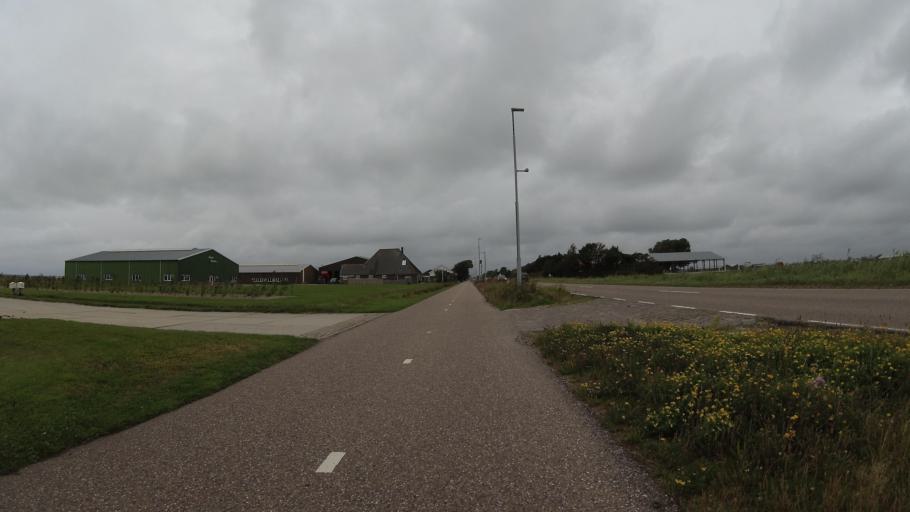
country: NL
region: North Holland
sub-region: Gemeente Den Helder
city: Den Helder
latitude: 52.9067
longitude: 4.7529
